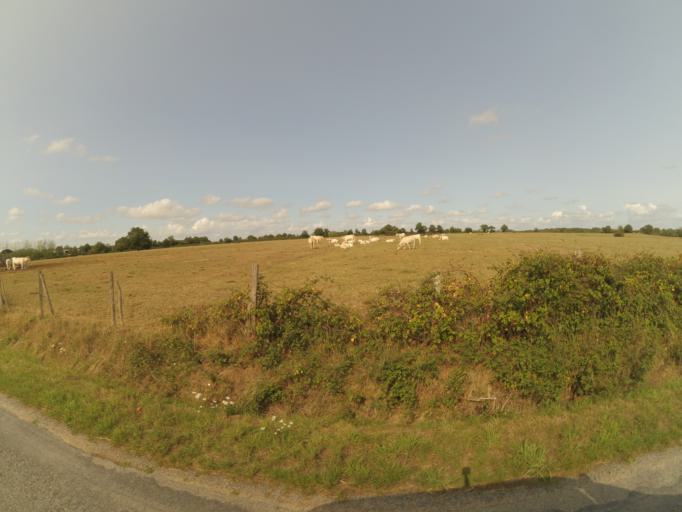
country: FR
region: Pays de la Loire
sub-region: Departement de la Loire-Atlantique
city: Boussay
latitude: 47.0400
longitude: -1.1592
